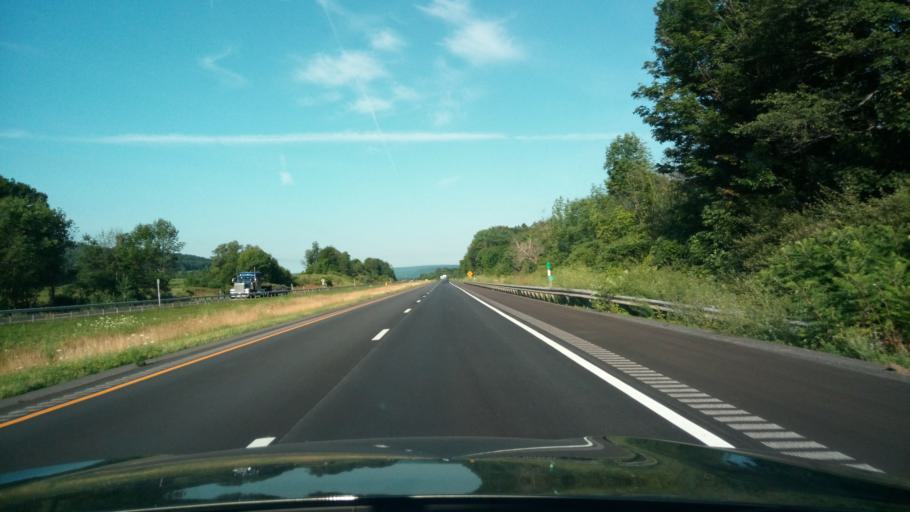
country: US
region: New York
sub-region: Steuben County
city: Wayland
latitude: 42.5351
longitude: -77.6291
